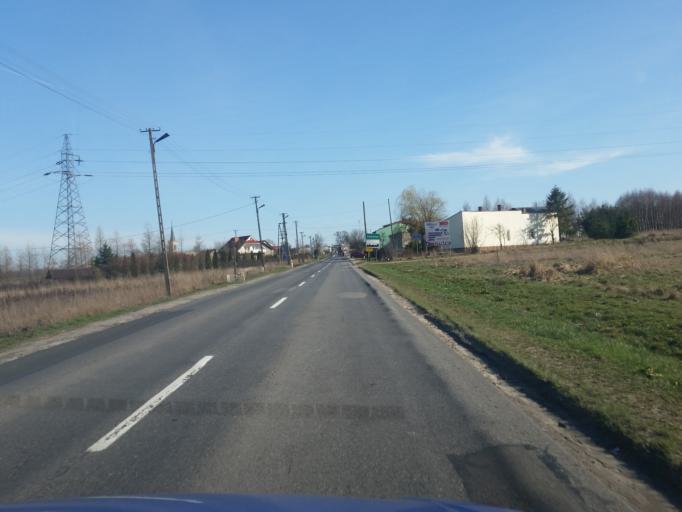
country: PL
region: Lodz Voivodeship
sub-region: Powiat radomszczanski
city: Kamiensk
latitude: 51.2084
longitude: 19.4908
